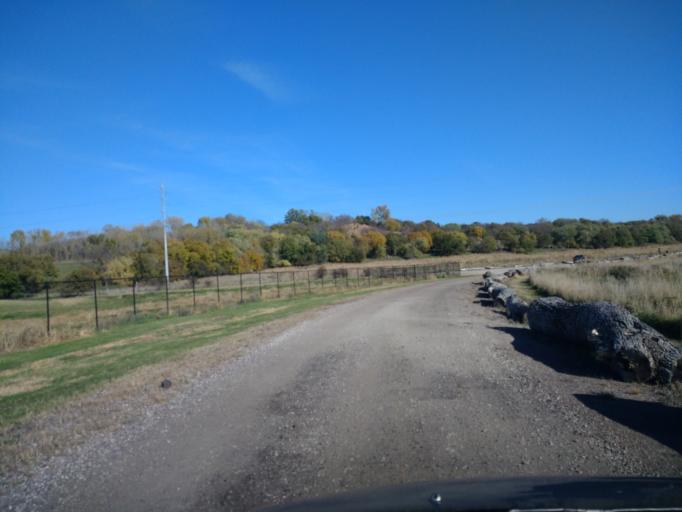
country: US
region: Iowa
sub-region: Woodbury County
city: Sergeant Bluff
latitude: 42.4500
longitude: -96.3712
